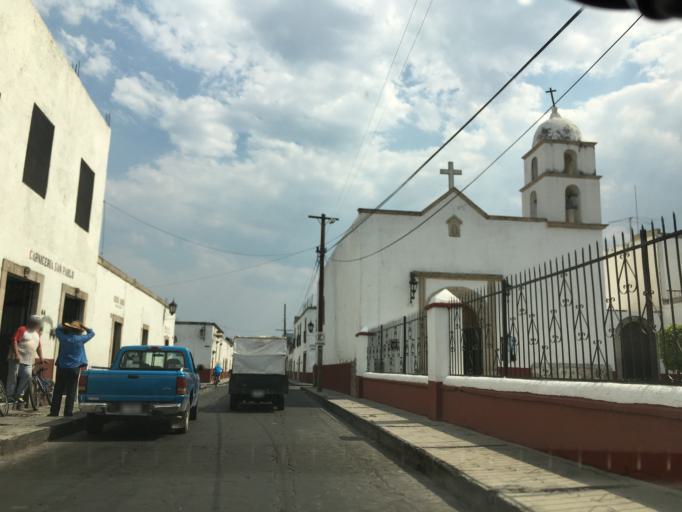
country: MX
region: Michoacan
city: Cuitzeo del Porvenir
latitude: 19.9680
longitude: -101.1407
